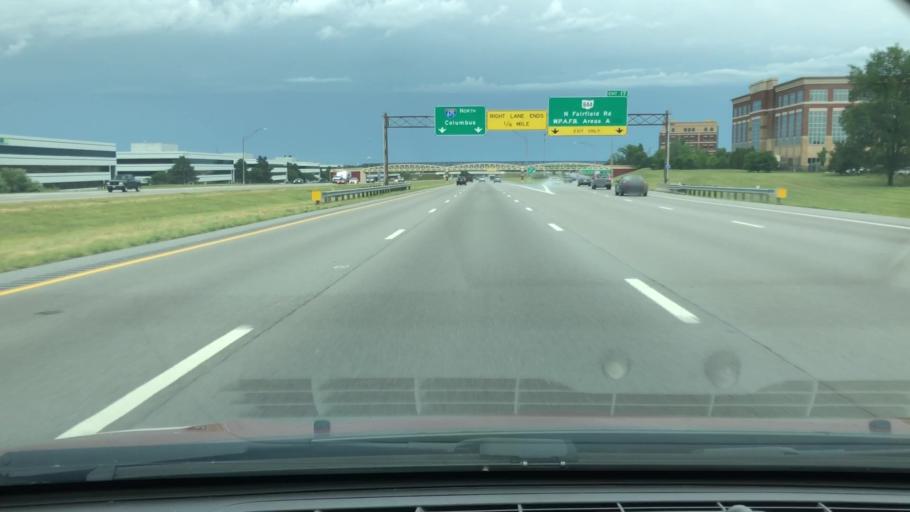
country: US
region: Ohio
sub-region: Greene County
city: Wright-Patterson AFB
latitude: 39.7736
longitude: -84.0650
